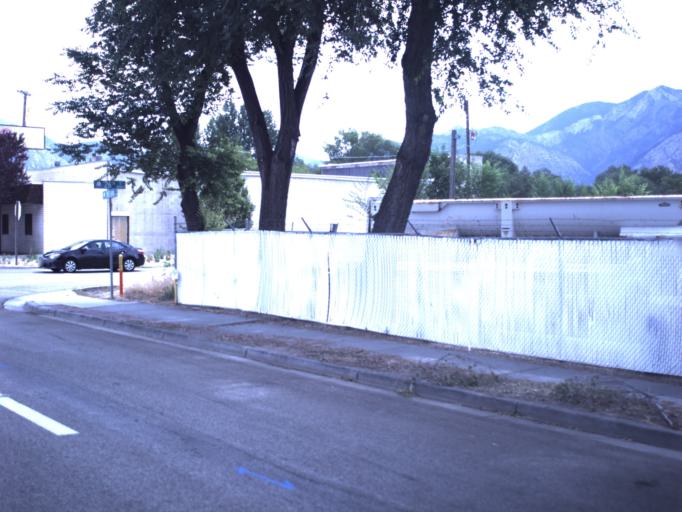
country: US
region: Utah
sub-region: Weber County
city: Ogden
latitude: 41.2202
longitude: -112.0040
